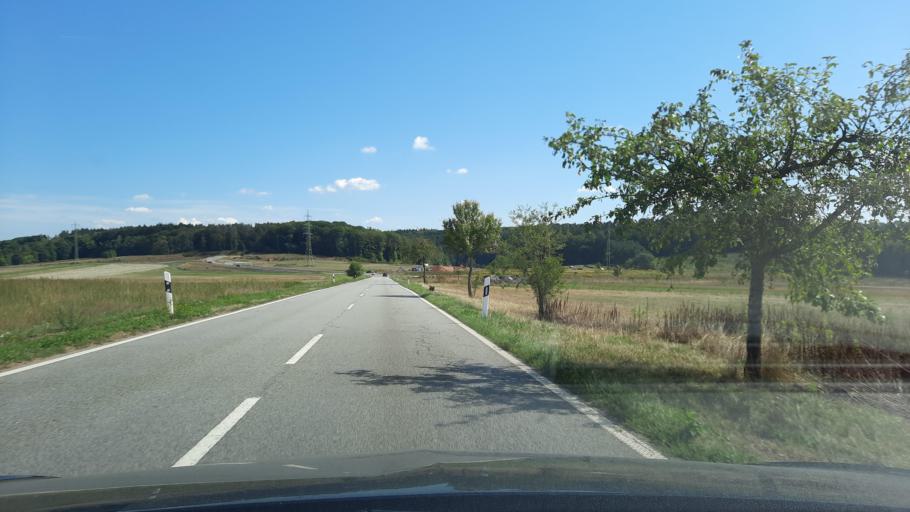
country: DE
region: Rheinland-Pfalz
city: Tawern
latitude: 49.6728
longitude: 6.5280
